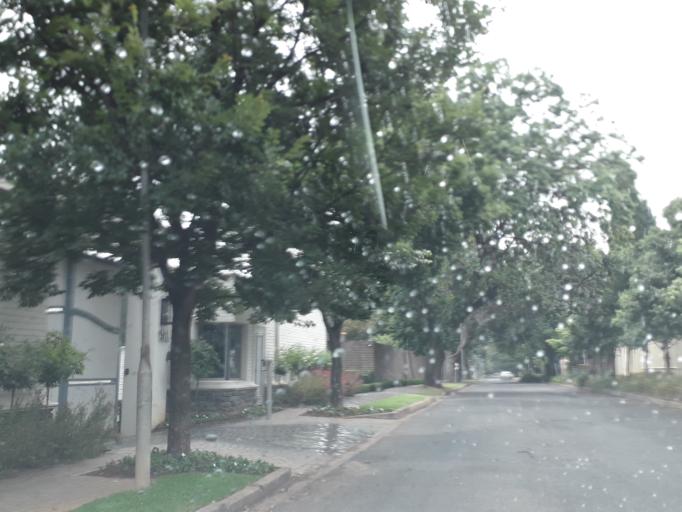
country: ZA
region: Gauteng
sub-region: City of Johannesburg Metropolitan Municipality
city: Johannesburg
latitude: -26.1371
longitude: 28.0386
